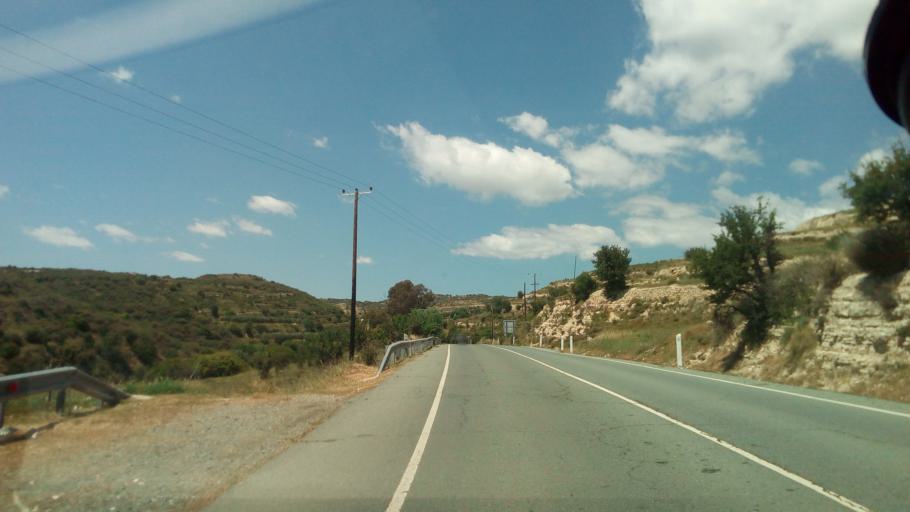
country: CY
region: Limassol
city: Pachna
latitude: 34.7898
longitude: 32.8247
